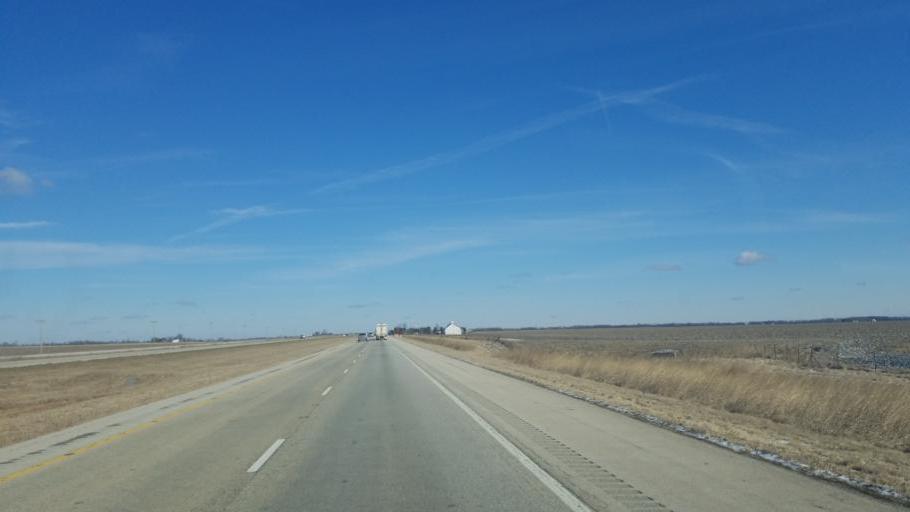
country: US
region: Illinois
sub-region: Sangamon County
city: Divernon
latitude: 39.4803
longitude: -89.6445
